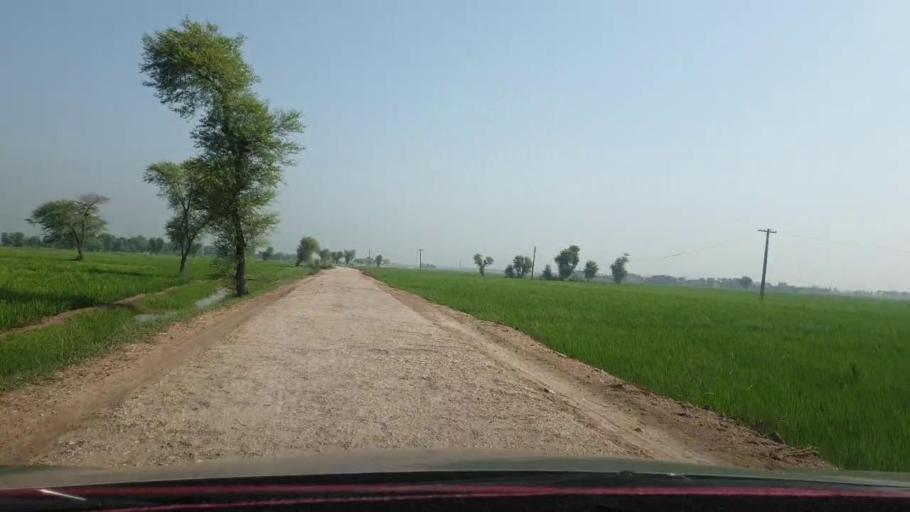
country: PK
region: Sindh
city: Nasirabad
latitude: 27.4893
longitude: 67.9270
